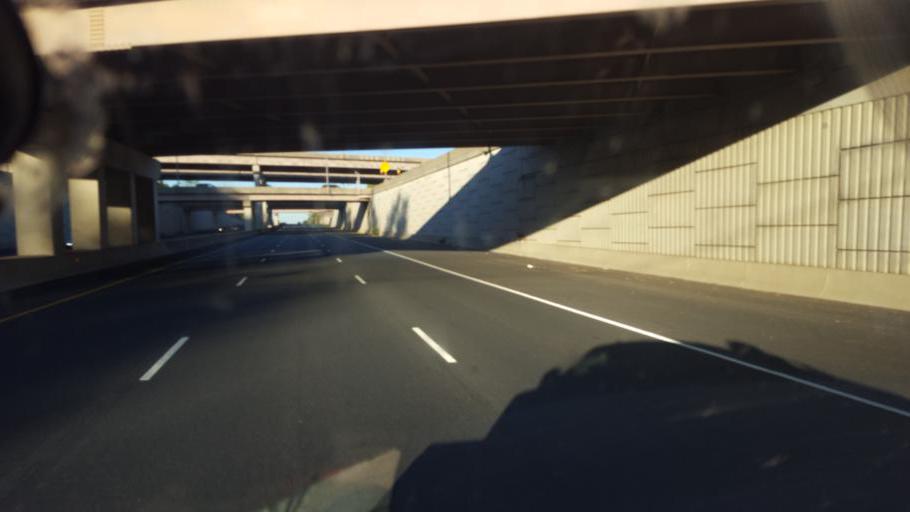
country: US
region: Virginia
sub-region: Fairfax County
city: Greenbriar
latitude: 38.8455
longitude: -77.3735
